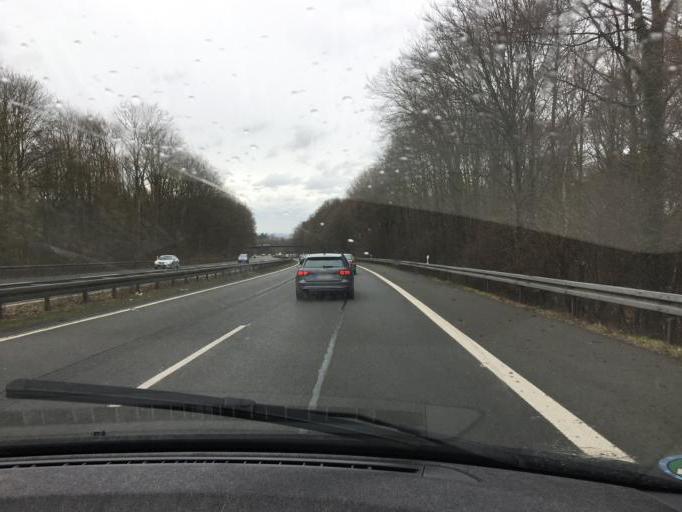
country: DE
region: North Rhine-Westphalia
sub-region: Regierungsbezirk Arnsberg
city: Dortmund
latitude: 51.4496
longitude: 7.4864
